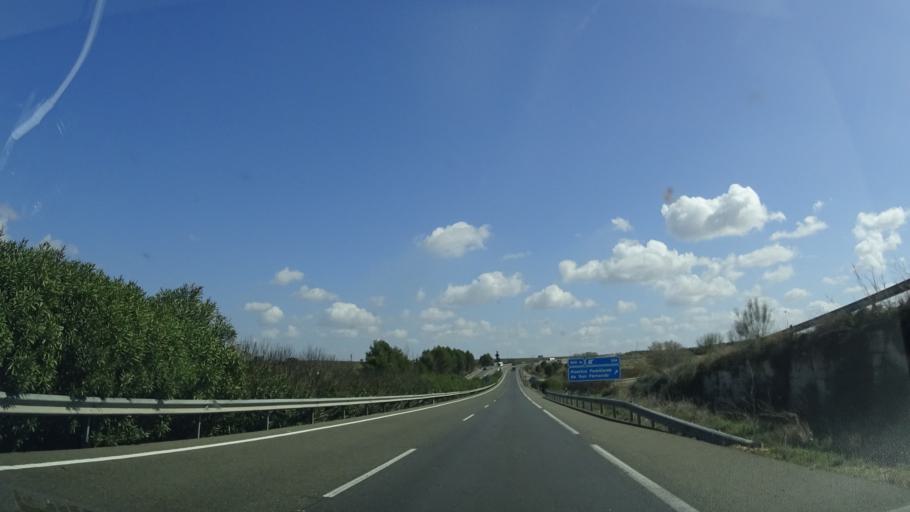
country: ES
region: Andalusia
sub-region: Province of Cordoba
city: Montoro
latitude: 38.0071
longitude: -4.3546
